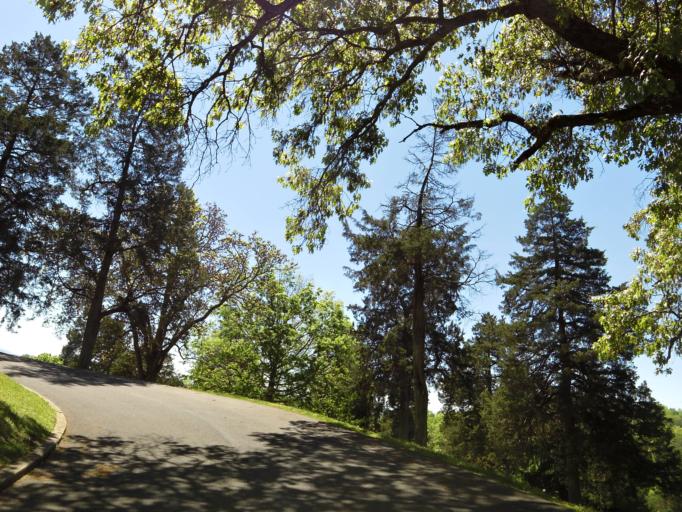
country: US
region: Tennessee
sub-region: Greene County
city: Greeneville
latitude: 36.1555
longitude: -82.8381
